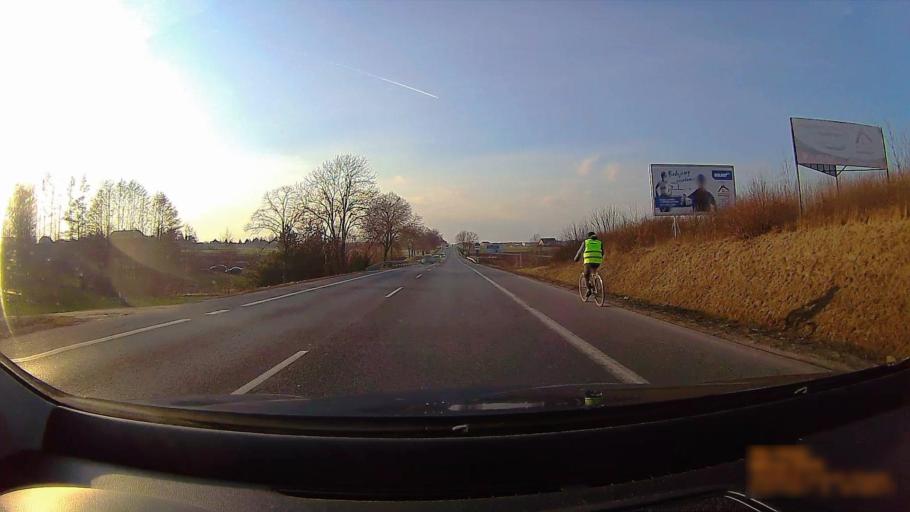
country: PL
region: Greater Poland Voivodeship
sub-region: Konin
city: Konin
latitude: 52.1920
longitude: 18.3262
